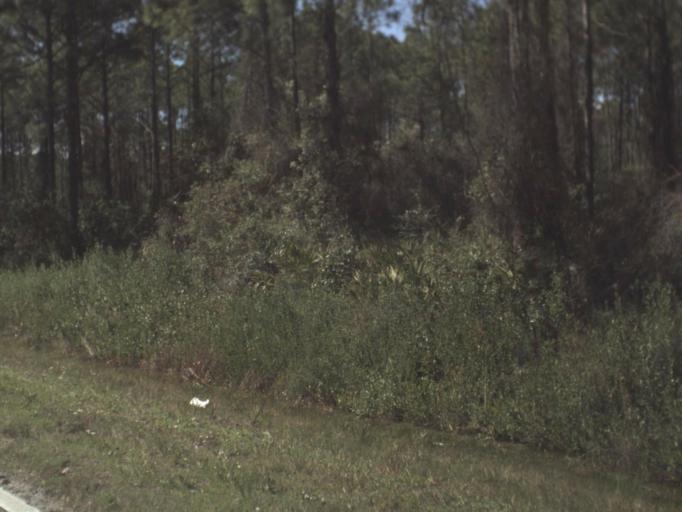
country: US
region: Florida
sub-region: Franklin County
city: Carrabelle
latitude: 29.9137
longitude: -84.5280
